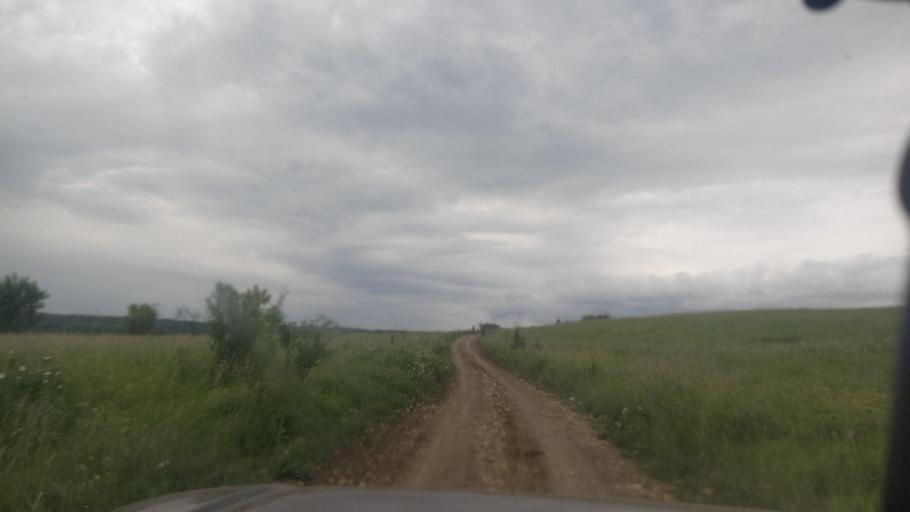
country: RU
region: Krasnodarskiy
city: Peredovaya
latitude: 44.0698
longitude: 41.3628
